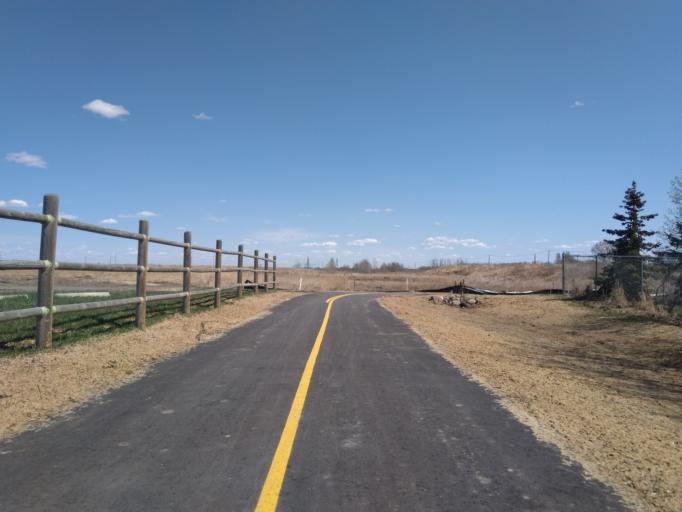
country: CA
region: Alberta
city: Chestermere
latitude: 50.9539
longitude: -113.9108
